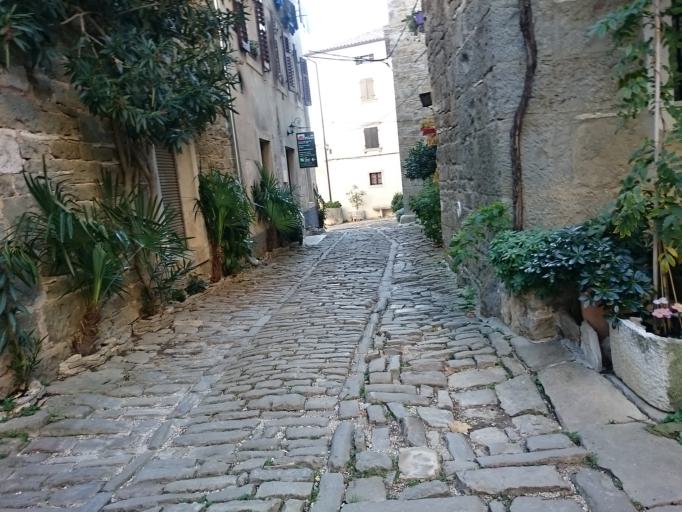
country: HR
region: Istarska
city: Buje
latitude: 45.3789
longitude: 13.7225
